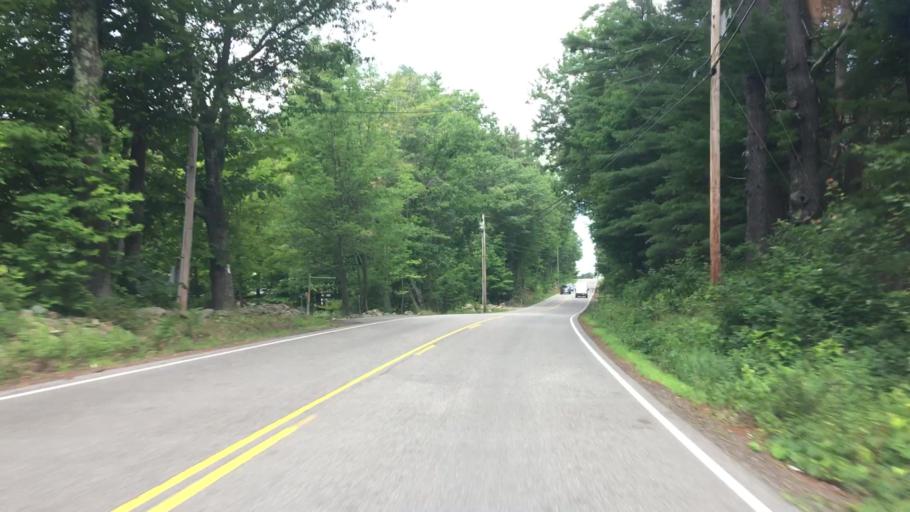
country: US
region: New Hampshire
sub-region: Belknap County
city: Laconia
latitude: 43.5818
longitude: -71.5139
